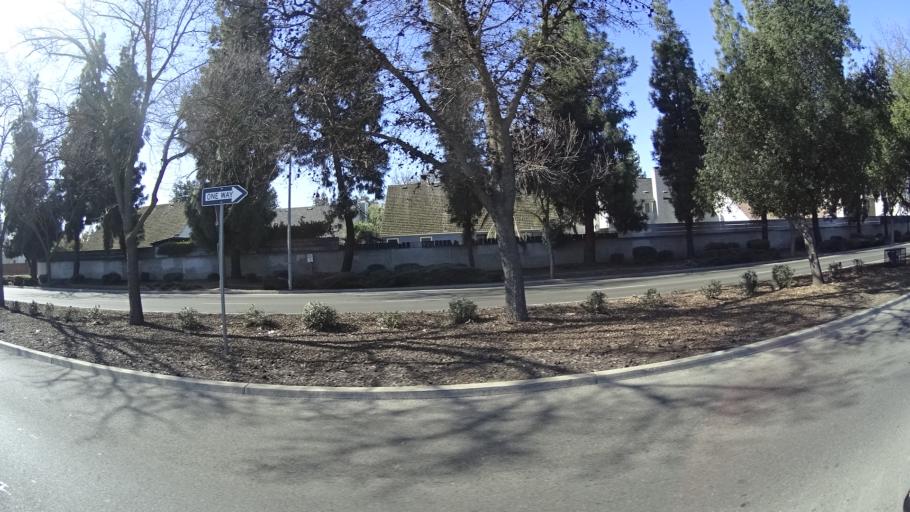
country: US
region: California
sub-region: Fresno County
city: West Park
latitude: 36.8177
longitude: -119.8651
